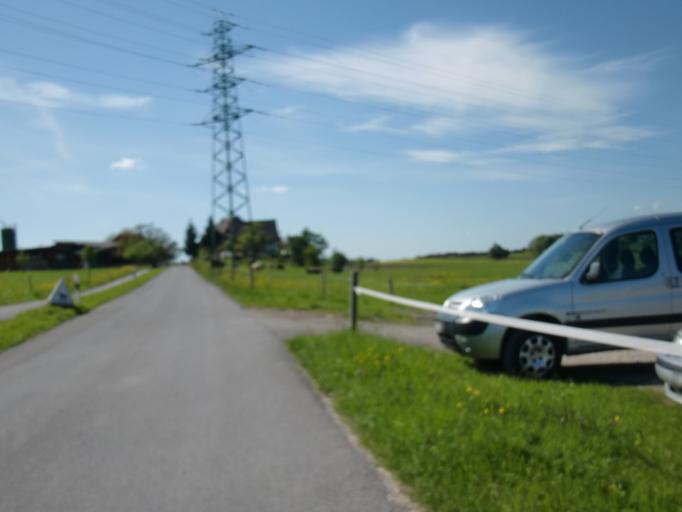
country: CH
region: Zurich
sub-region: Bezirk Hinwil
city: Wolfhausen
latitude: 47.2651
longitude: 8.7998
